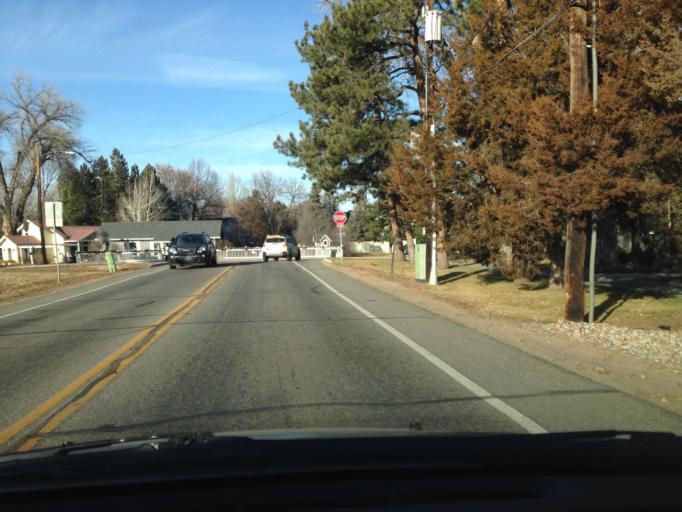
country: US
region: Colorado
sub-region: Boulder County
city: Niwot
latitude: 40.1010
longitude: -105.1691
